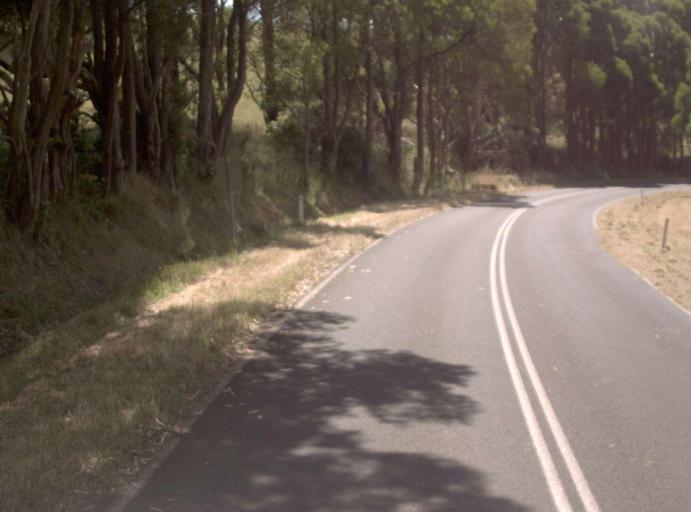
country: AU
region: Victoria
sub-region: Baw Baw
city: Warragul
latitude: -38.2648
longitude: 145.8937
